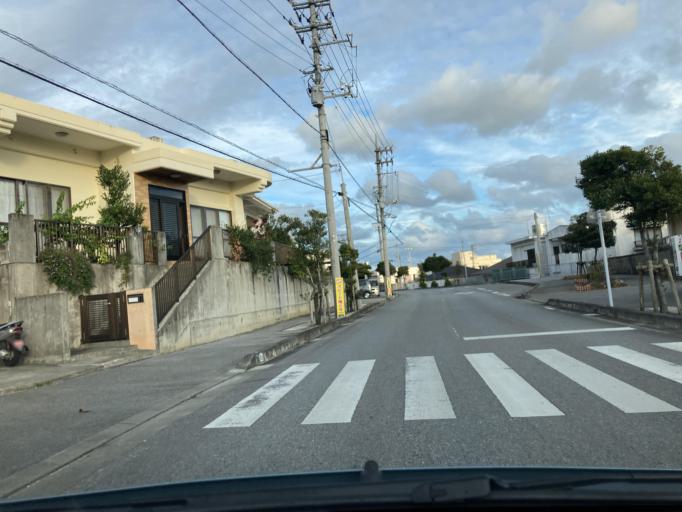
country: JP
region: Okinawa
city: Itoman
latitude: 26.1498
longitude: 127.7001
